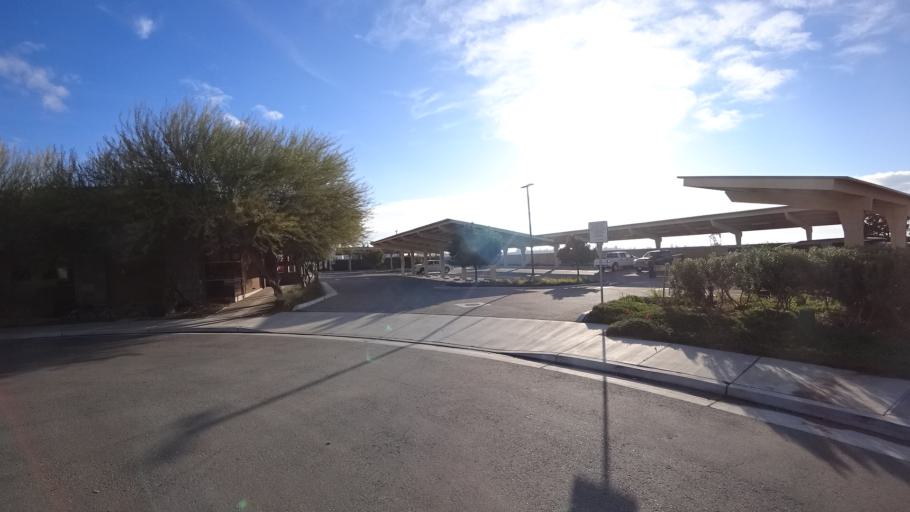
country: US
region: California
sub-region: Kern County
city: Rosedale
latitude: 35.3114
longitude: -119.1322
